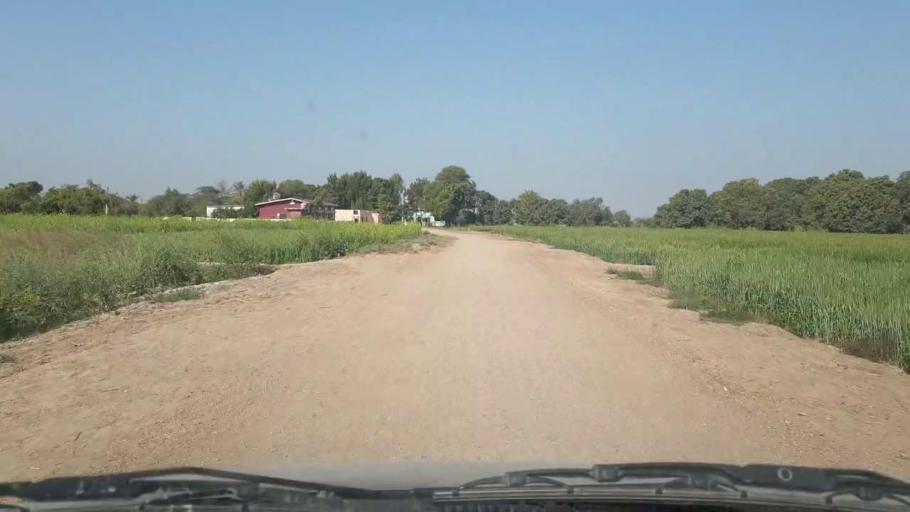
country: PK
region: Sindh
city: Samaro
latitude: 25.2998
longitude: 69.2922
